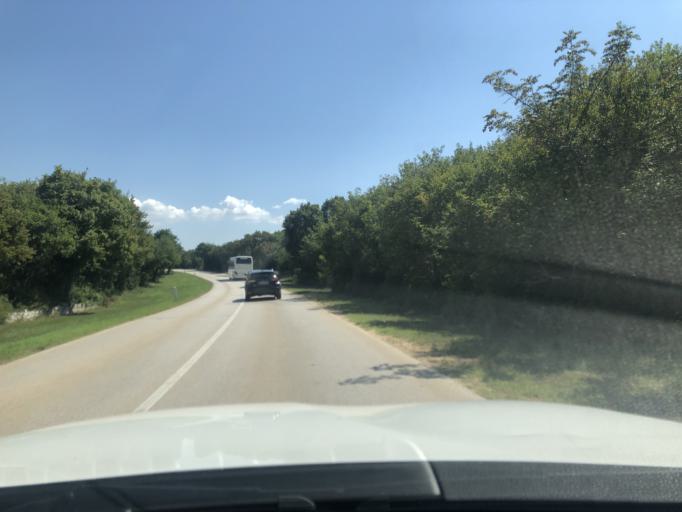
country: HR
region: Istarska
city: Vodnjan
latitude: 45.0370
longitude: 13.7835
